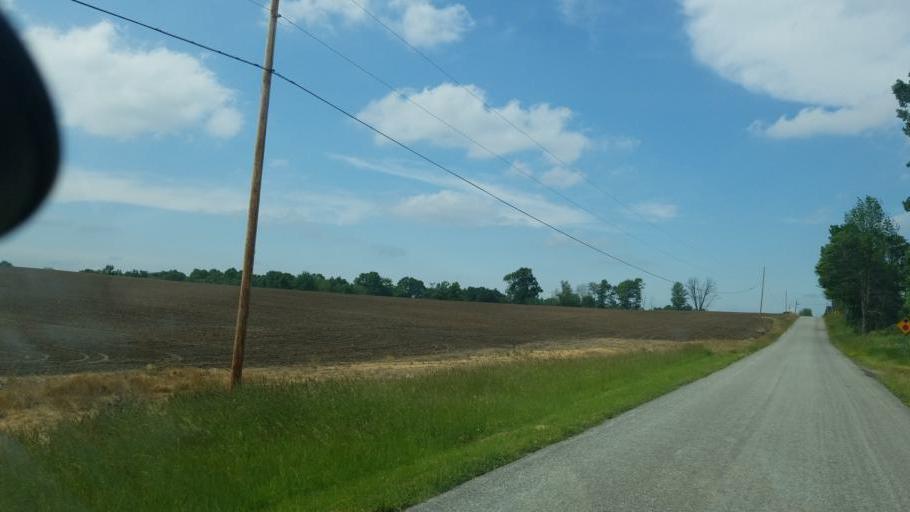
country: US
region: Ohio
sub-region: Knox County
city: Oak Hill
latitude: 40.2892
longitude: -82.1831
